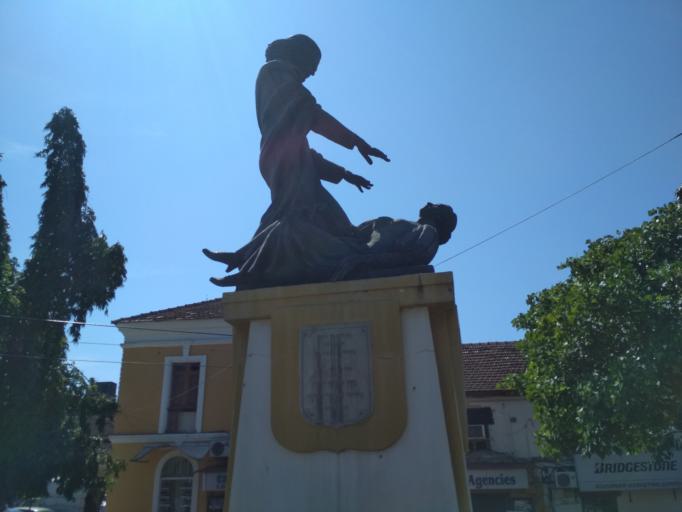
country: IN
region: Goa
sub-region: North Goa
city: Panaji
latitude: 15.5007
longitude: 73.8295
